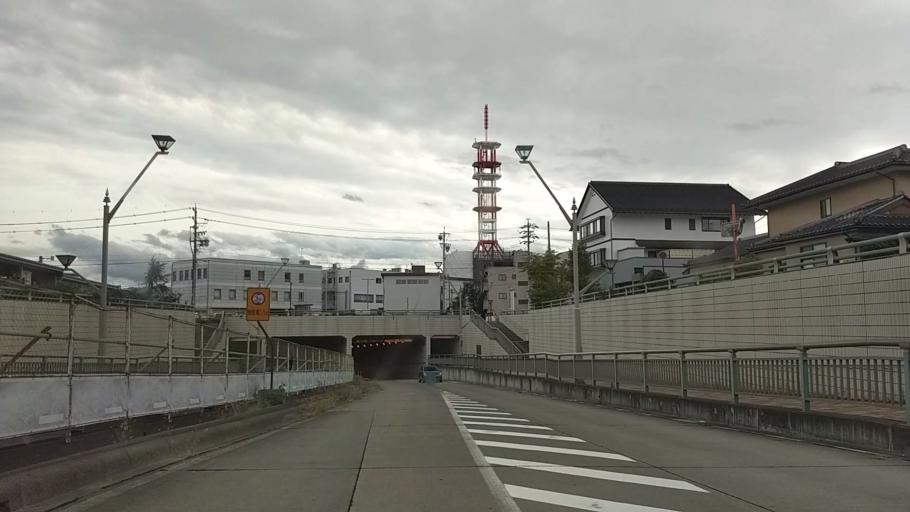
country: JP
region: Nagano
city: Nagano-shi
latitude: 36.6420
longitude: 138.1841
